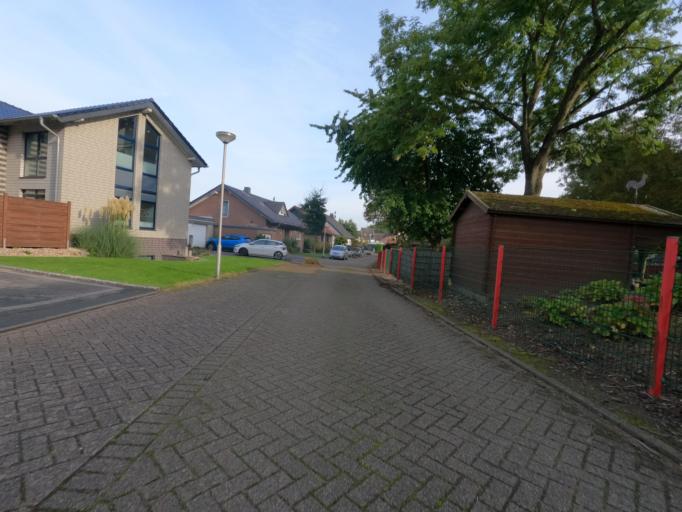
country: DE
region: North Rhine-Westphalia
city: Huckelhoven
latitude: 51.0183
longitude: 6.1750
